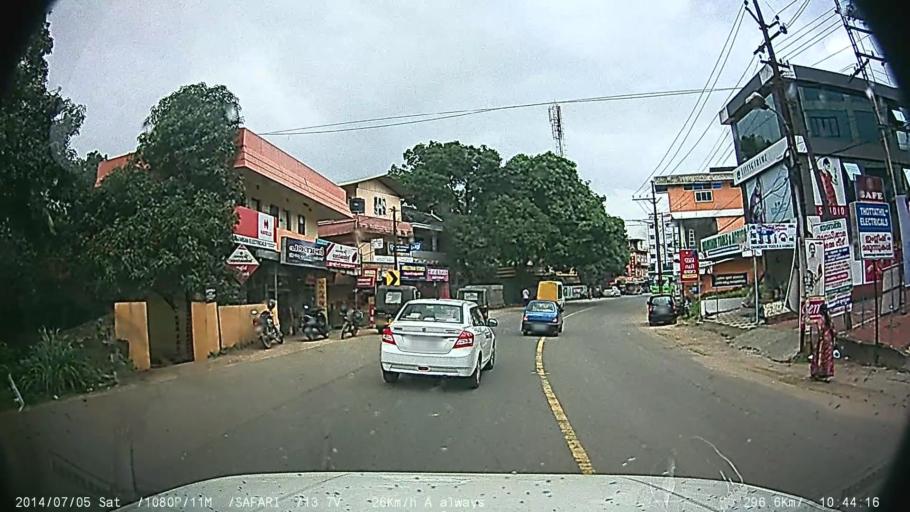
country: IN
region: Kerala
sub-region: Ernakulam
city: Muvattupula
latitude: 9.9799
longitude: 76.5846
